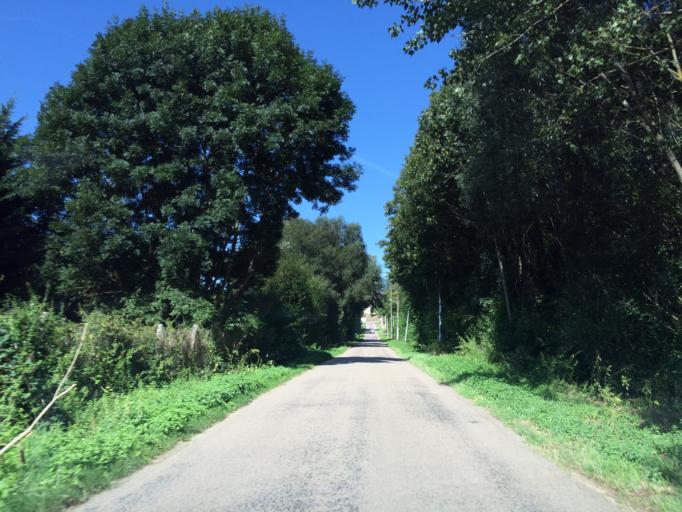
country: FR
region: Bourgogne
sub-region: Departement de l'Yonne
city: Aillant-sur-Tholon
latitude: 47.8629
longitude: 3.3964
